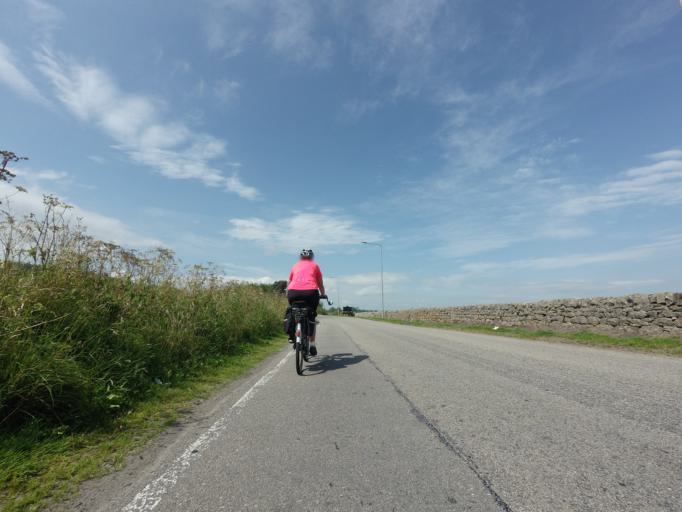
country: GB
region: Scotland
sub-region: Highland
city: Tain
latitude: 57.8171
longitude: -4.0681
